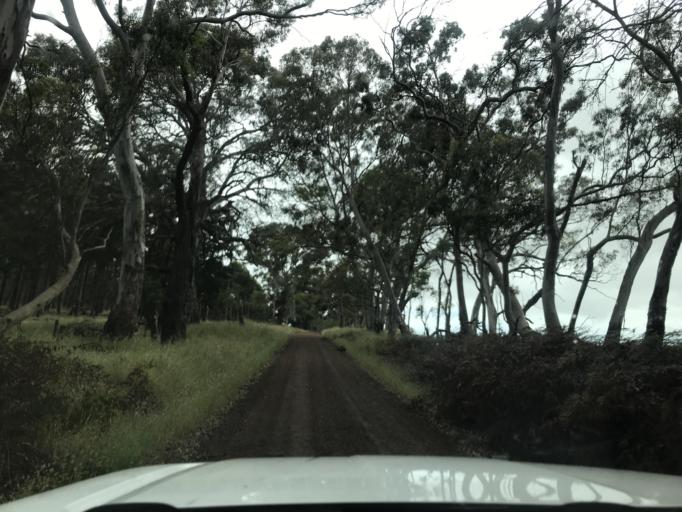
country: AU
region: South Australia
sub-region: Wattle Range
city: Penola
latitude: -37.2345
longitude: 141.4394
